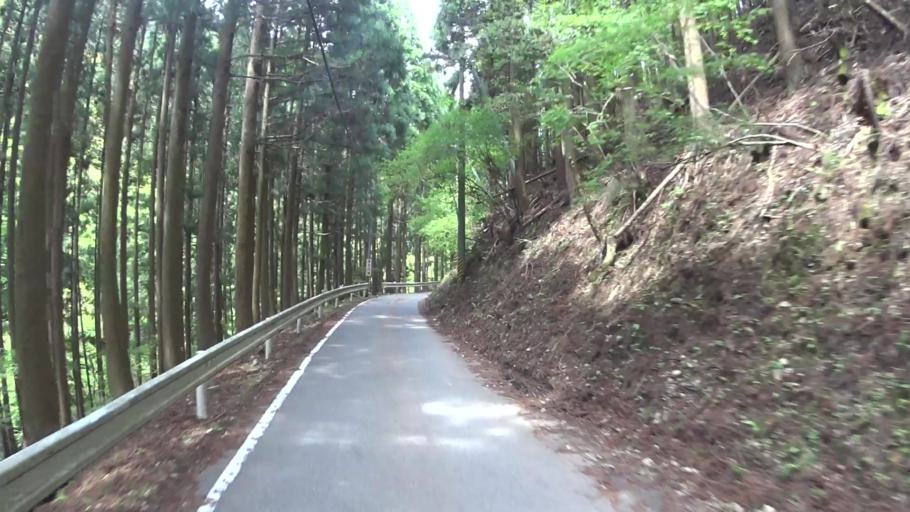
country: JP
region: Kyoto
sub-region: Kyoto-shi
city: Kamigyo-ku
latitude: 35.1727
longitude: 135.7427
